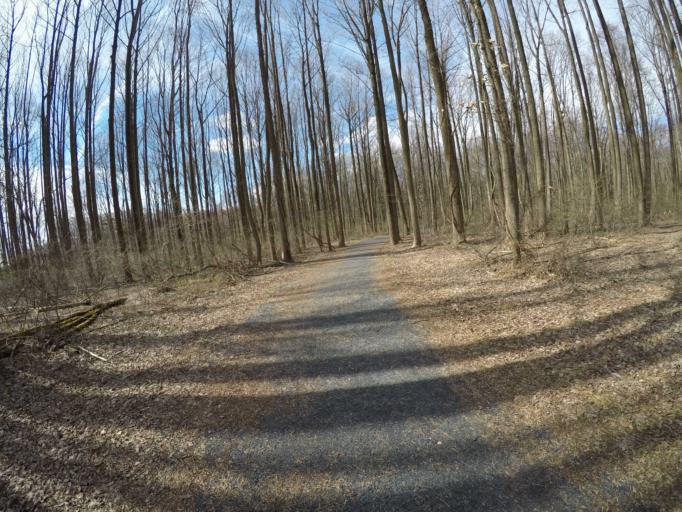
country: US
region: Maryland
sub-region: Harford County
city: Bel Air South
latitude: 39.4866
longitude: -76.3211
